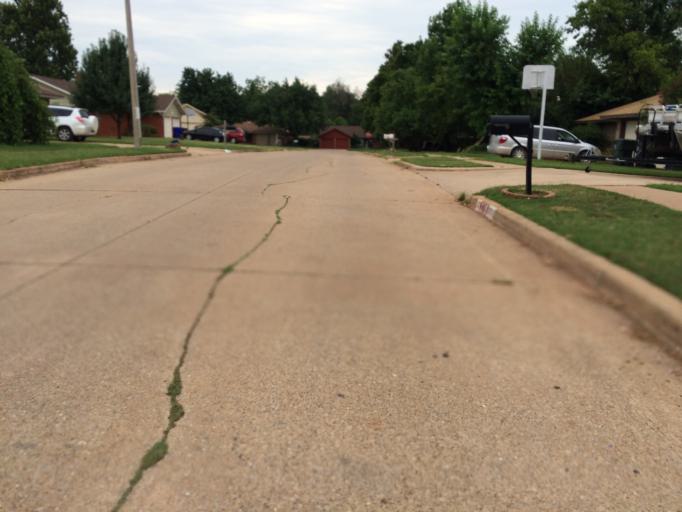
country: US
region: Oklahoma
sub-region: Cleveland County
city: Norman
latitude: 35.2525
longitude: -97.4330
